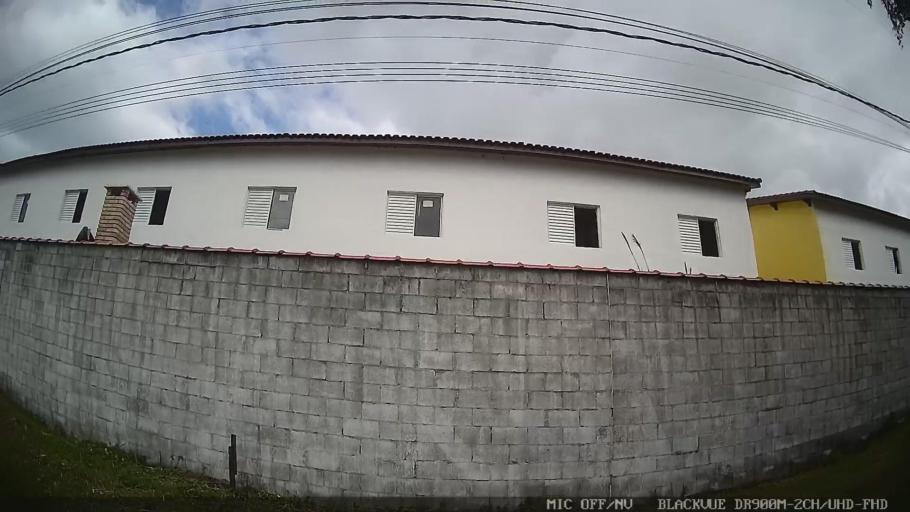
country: BR
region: Sao Paulo
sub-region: Itanhaem
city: Itanhaem
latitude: -24.1975
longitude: -46.8360
